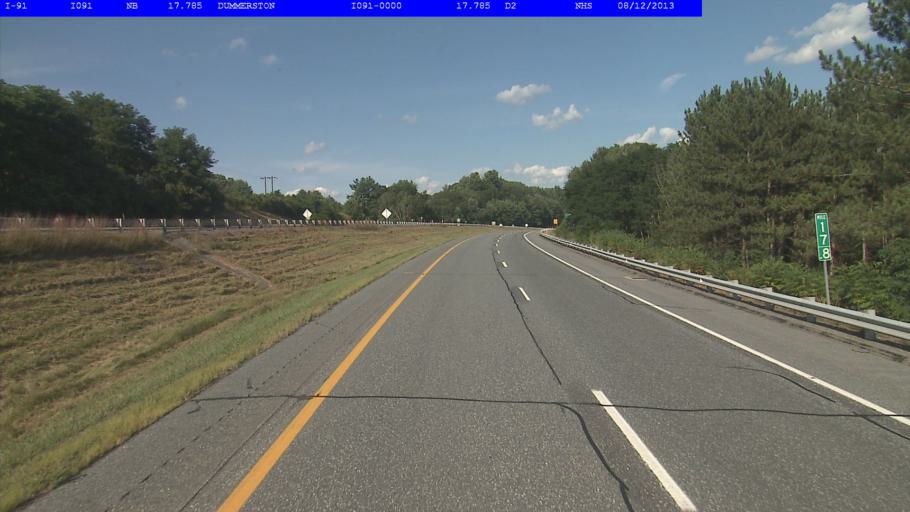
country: US
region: New Hampshire
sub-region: Cheshire County
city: Westmoreland
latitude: 42.9626
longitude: -72.5272
